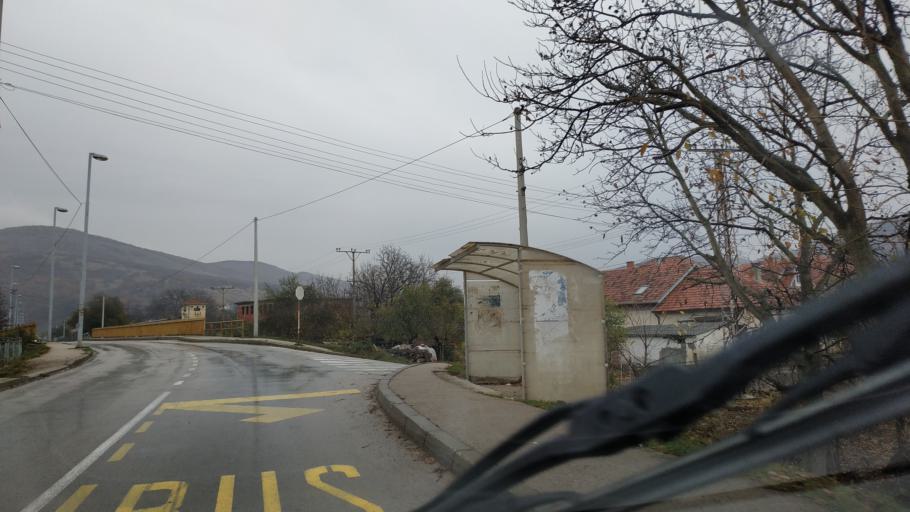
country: RS
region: Central Serbia
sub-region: Pirotski Okrug
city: Dimitrovgrad
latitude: 43.0116
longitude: 22.7525
